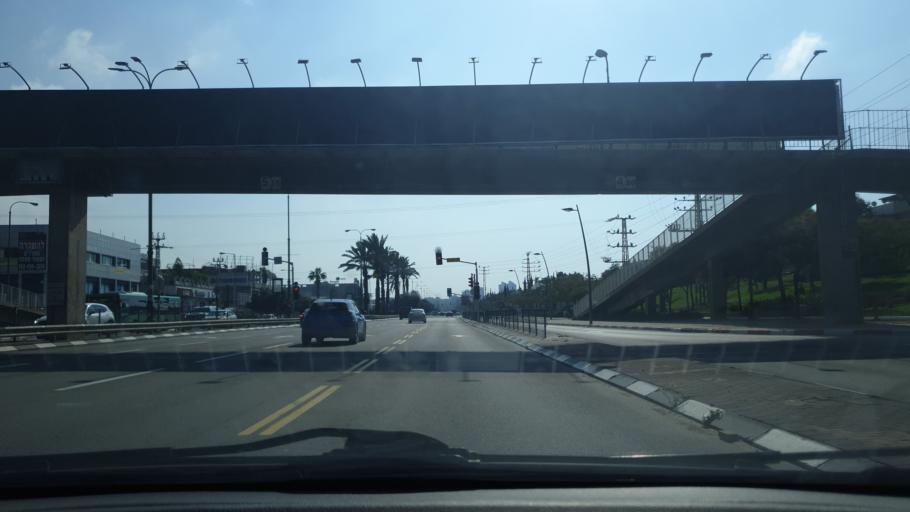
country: IL
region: Central District
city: Bet Dagan
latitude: 31.9843
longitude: 34.8104
